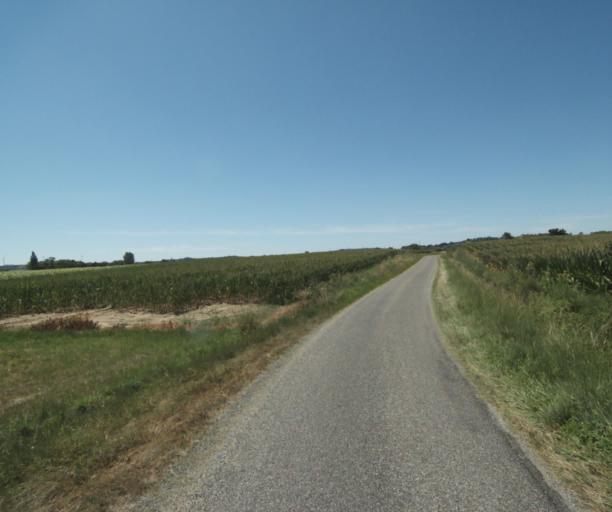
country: FR
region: Midi-Pyrenees
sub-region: Departement de la Haute-Garonne
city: Revel
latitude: 43.4862
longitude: 1.9506
